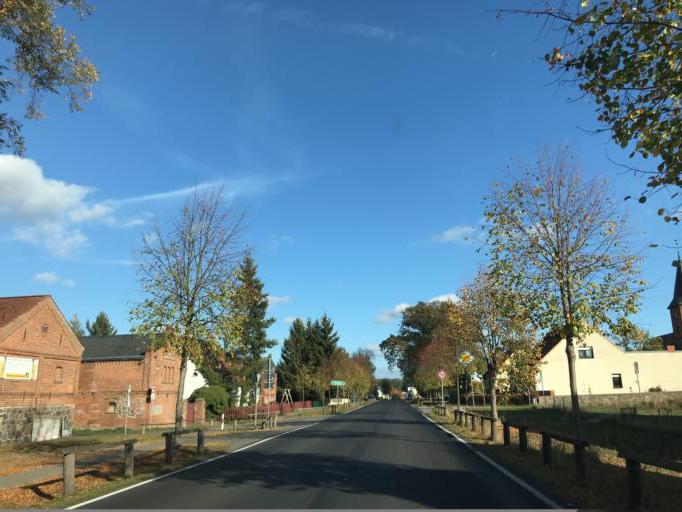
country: DE
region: Brandenburg
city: Schonermark
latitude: 53.0070
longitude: 13.1190
